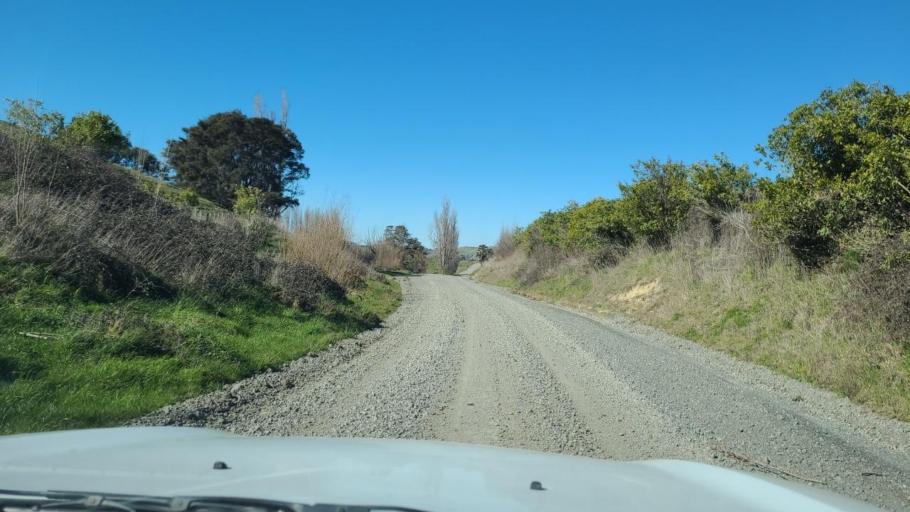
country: NZ
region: Hawke's Bay
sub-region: Napier City
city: Taradale
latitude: -39.4470
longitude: 176.5588
